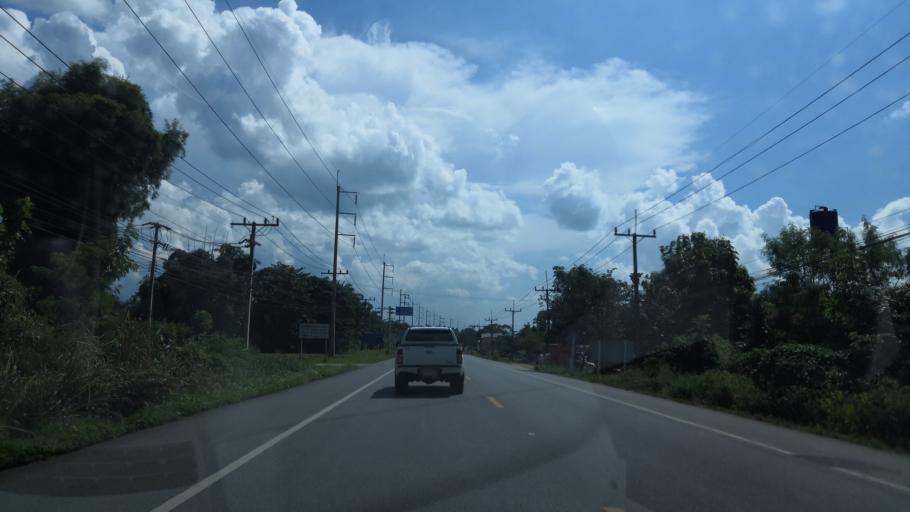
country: TH
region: Chiang Rai
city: Mae Suai
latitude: 19.6137
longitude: 99.5095
